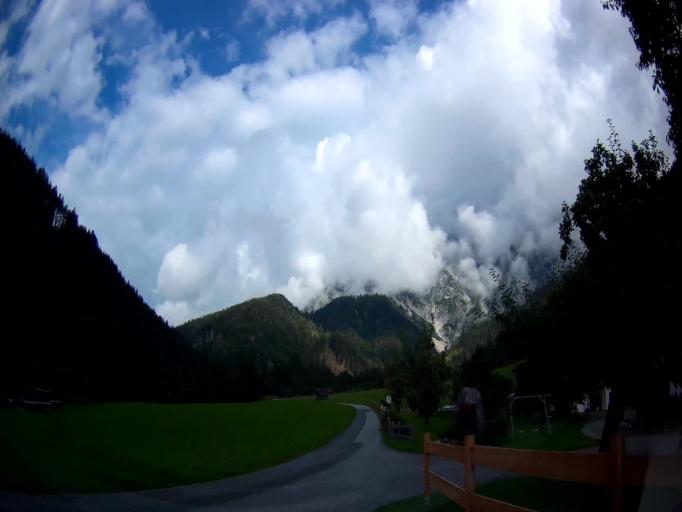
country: AT
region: Salzburg
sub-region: Politischer Bezirk Zell am See
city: Leogang
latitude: 47.4491
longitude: 12.7654
